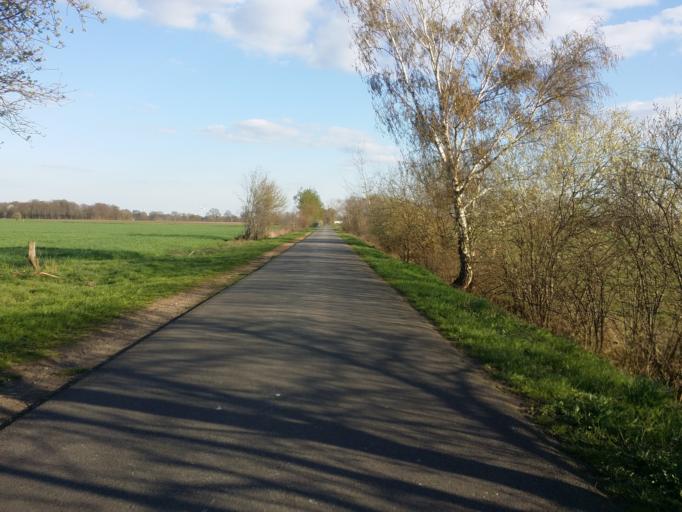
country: DE
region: Lower Saxony
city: Delmenhorst
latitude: 53.0121
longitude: 8.6304
